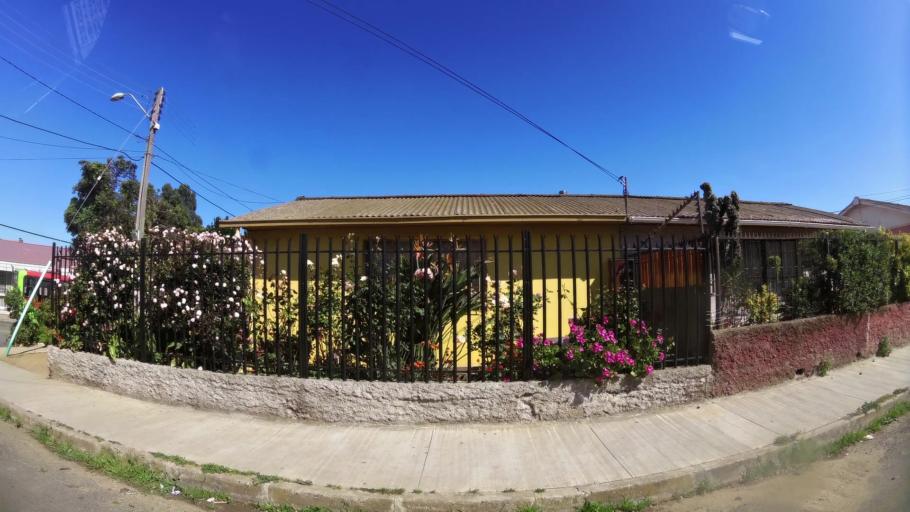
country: CL
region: Valparaiso
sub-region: Provincia de Valparaiso
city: Valparaiso
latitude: -33.0537
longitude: -71.6508
